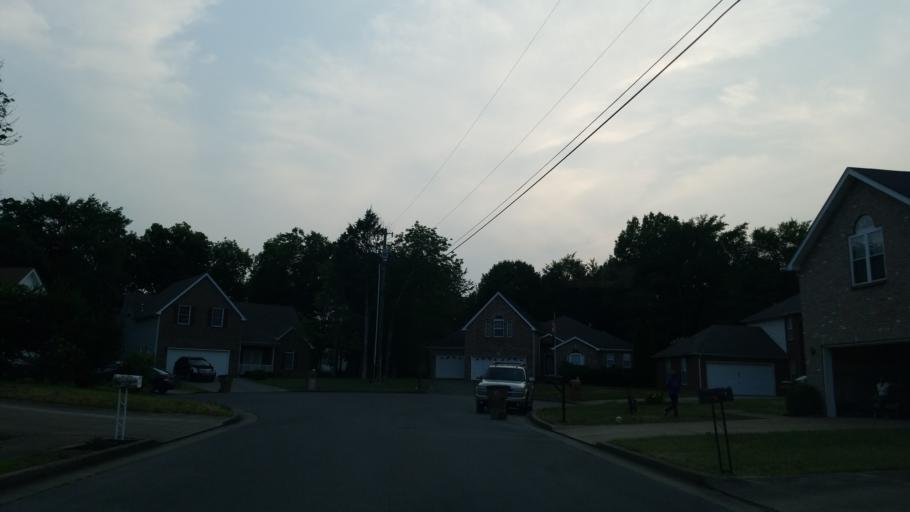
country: US
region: Tennessee
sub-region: Rutherford County
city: La Vergne
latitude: 36.0367
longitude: -86.5844
